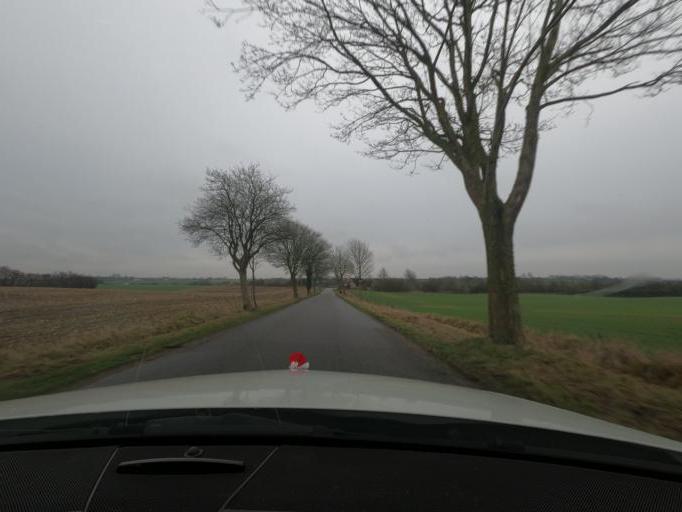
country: DK
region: South Denmark
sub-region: Haderslev Kommune
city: Haderslev
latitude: 55.1938
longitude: 9.4887
